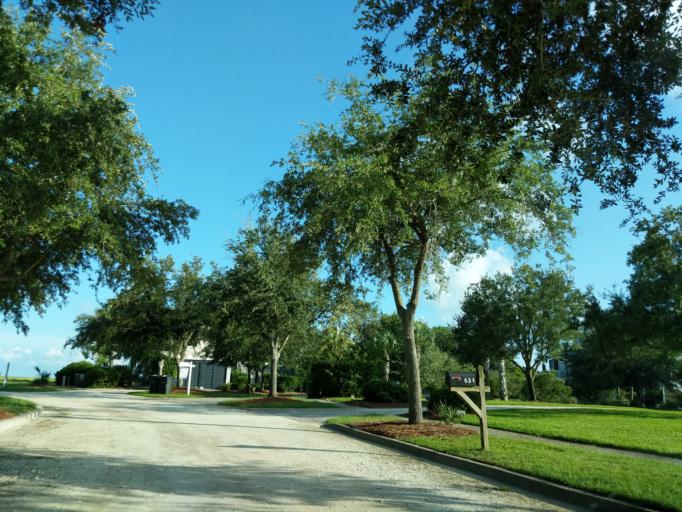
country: US
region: South Carolina
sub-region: Charleston County
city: Awendaw
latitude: 33.0797
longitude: -79.4588
